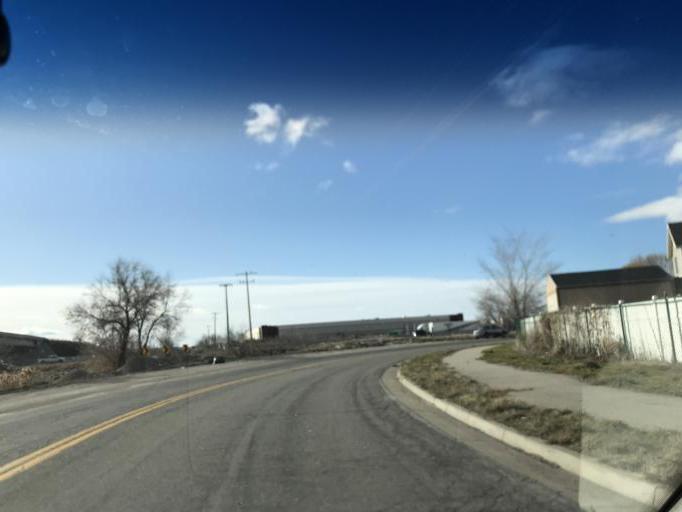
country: US
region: Utah
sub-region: Davis County
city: North Salt Lake
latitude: 40.8061
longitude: -111.9473
